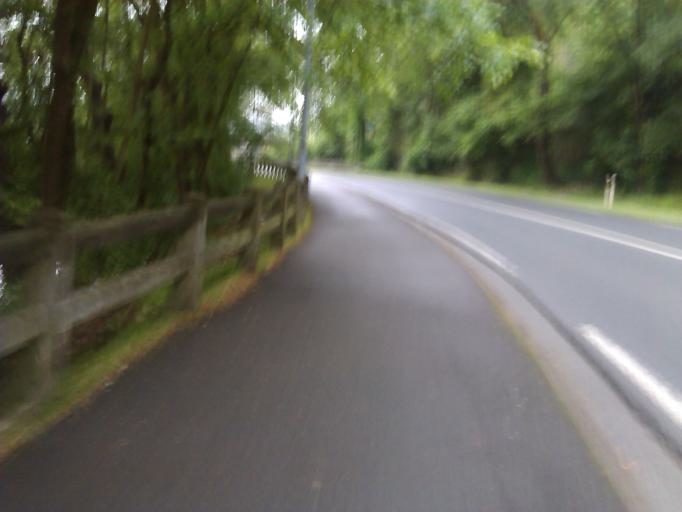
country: ES
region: Basque Country
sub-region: Provincia de Guipuzcoa
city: San Sebastian
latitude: 43.3058
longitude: -1.9659
